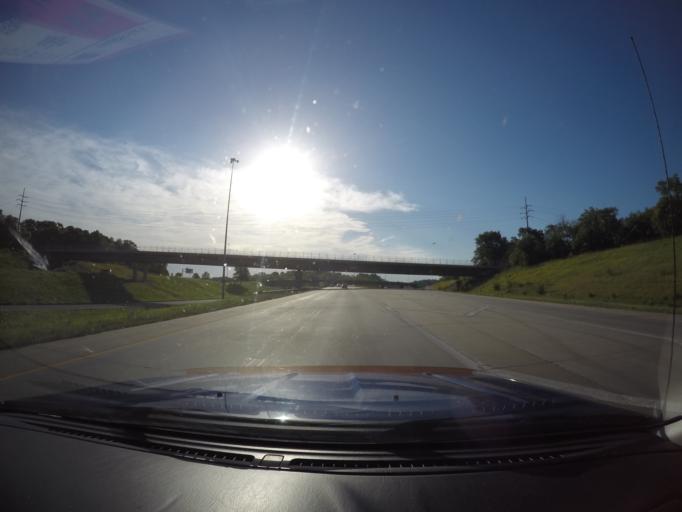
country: US
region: Kansas
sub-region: Wyandotte County
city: Kansas City
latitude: 39.1465
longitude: -94.6603
